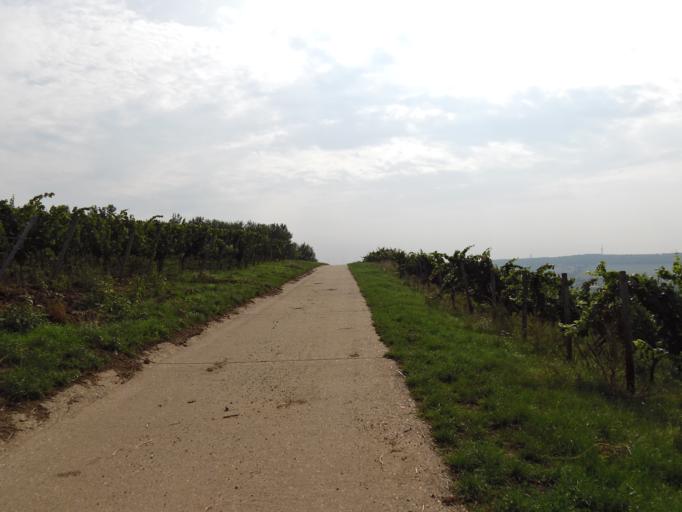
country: DE
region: Rheinland-Pfalz
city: Alzey
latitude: 49.7471
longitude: 8.0878
